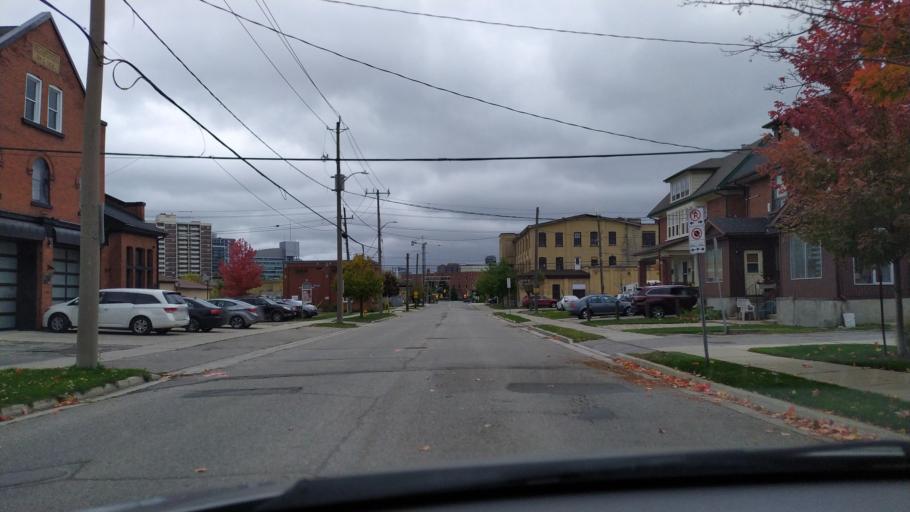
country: CA
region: Ontario
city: Waterloo
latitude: 43.4560
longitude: -80.4970
